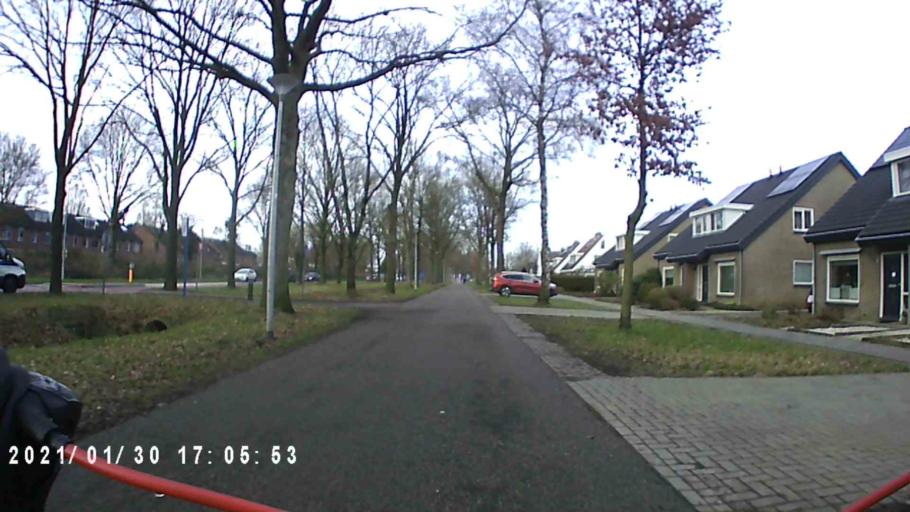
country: NL
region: Groningen
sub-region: Gemeente Leek
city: Leek
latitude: 53.1597
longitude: 6.3685
